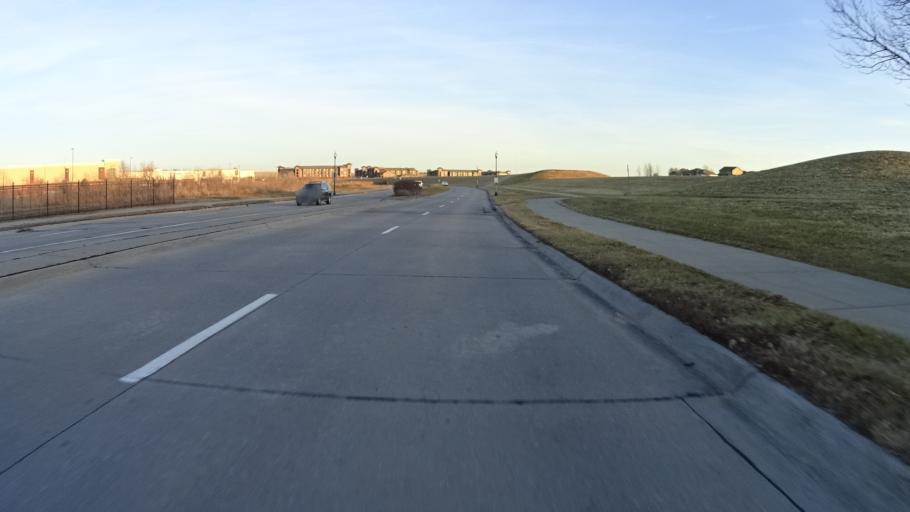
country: US
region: Nebraska
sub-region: Sarpy County
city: Papillion
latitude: 41.1326
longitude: -96.0337
